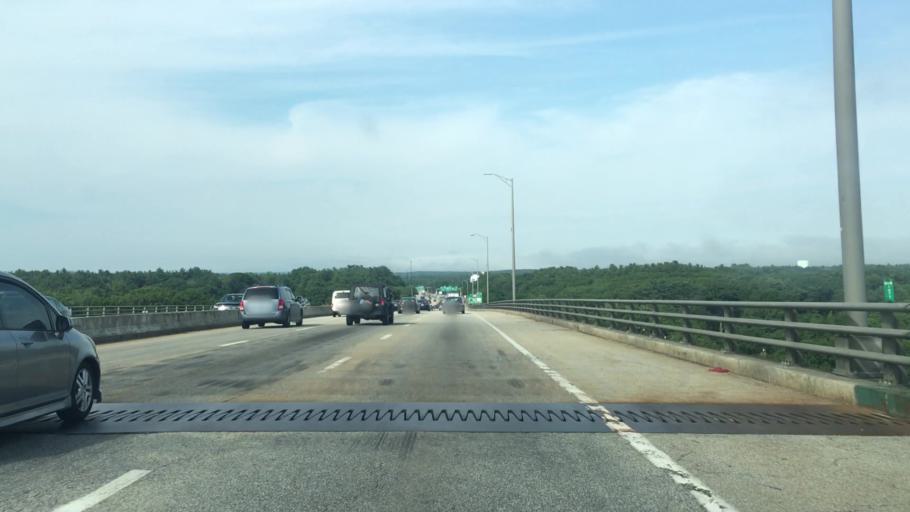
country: US
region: Maine
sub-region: York County
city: South Eliot
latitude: 43.0938
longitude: -70.7643
